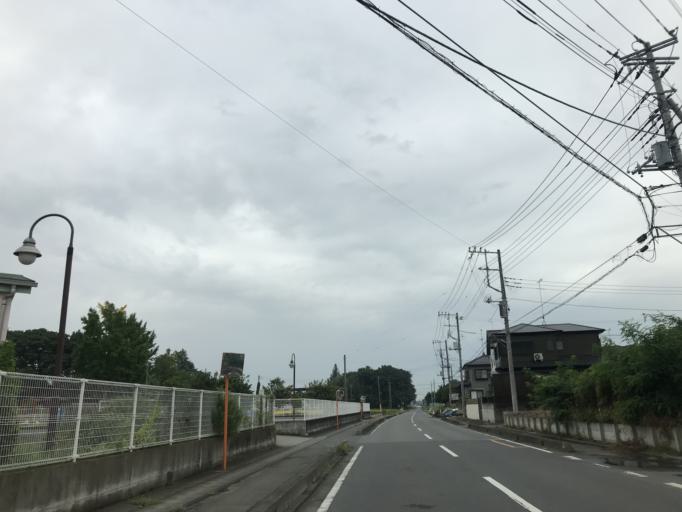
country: JP
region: Ibaraki
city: Sakai
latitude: 36.1201
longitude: 139.7918
